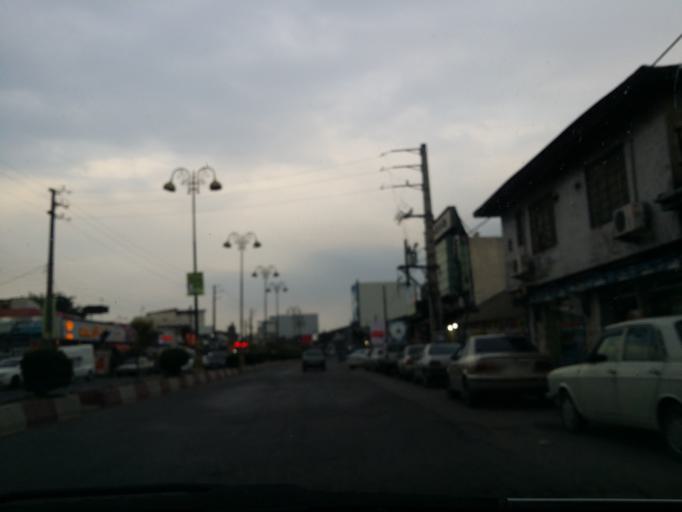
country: IR
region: Mazandaran
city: `Abbasabad
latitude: 36.7285
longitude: 51.1074
